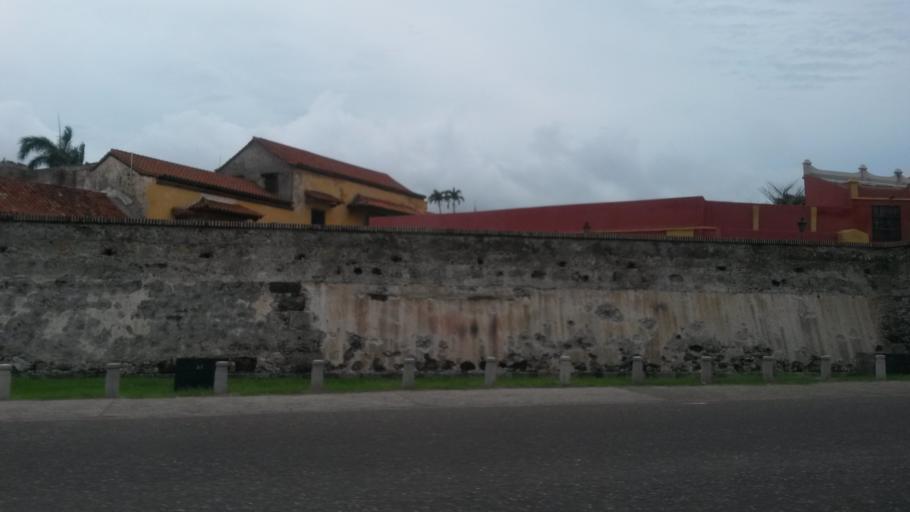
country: CO
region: Bolivar
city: Cartagena
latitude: 10.4267
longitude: -75.5520
